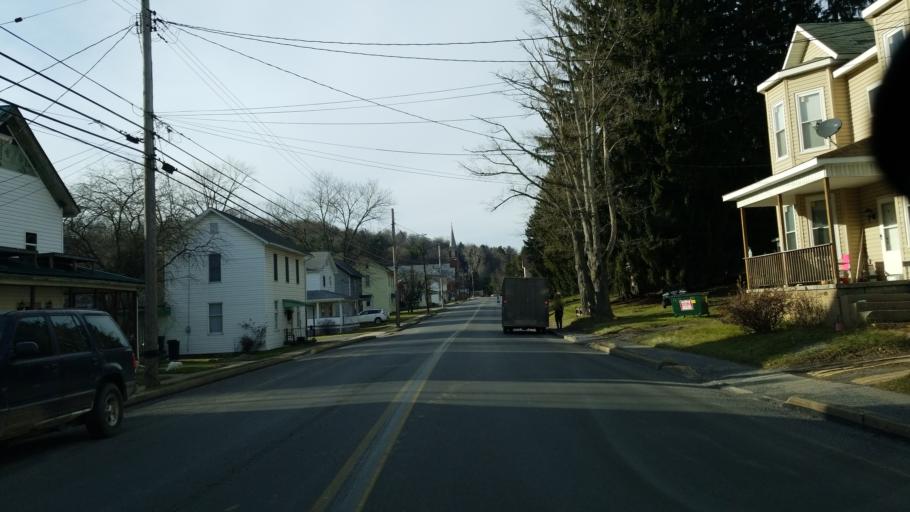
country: US
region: Pennsylvania
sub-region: Clearfield County
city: Curwensville
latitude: 40.9657
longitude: -78.6133
